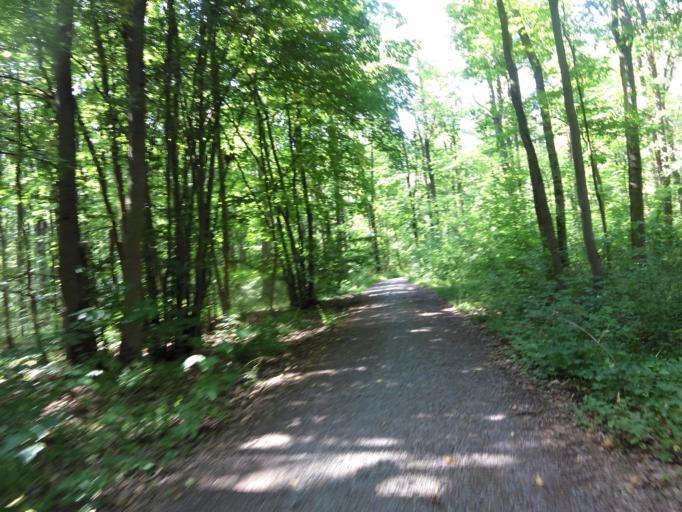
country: DE
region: Bavaria
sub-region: Regierungsbezirk Unterfranken
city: Estenfeld
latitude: 49.8341
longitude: 9.9770
